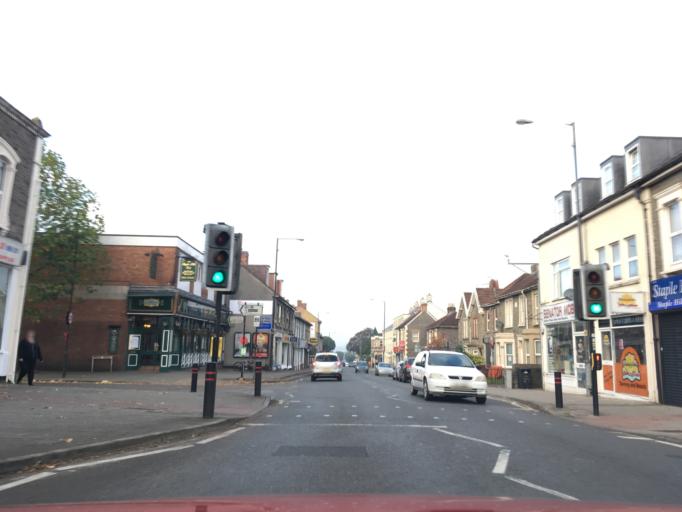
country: GB
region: England
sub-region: South Gloucestershire
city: Mangotsfield
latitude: 51.4812
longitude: -2.5087
